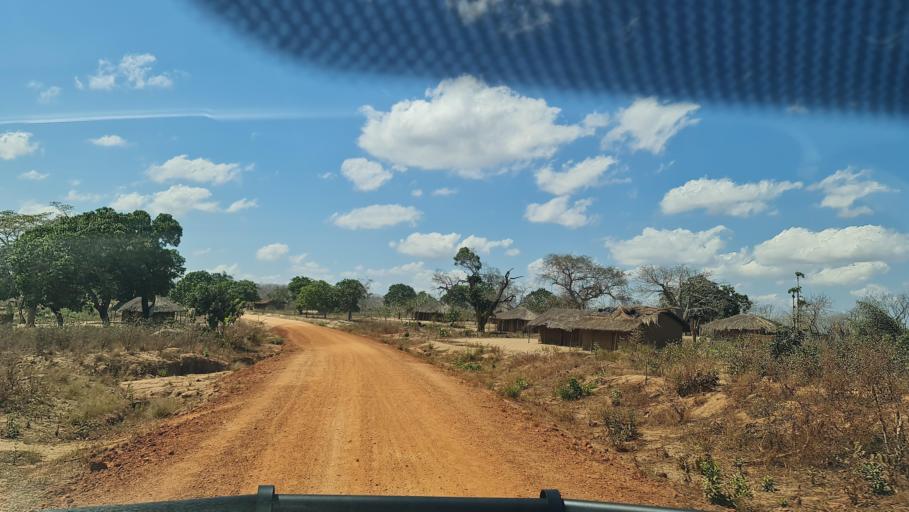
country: MZ
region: Nampula
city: Nacala
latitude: -14.1777
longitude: 40.2183
